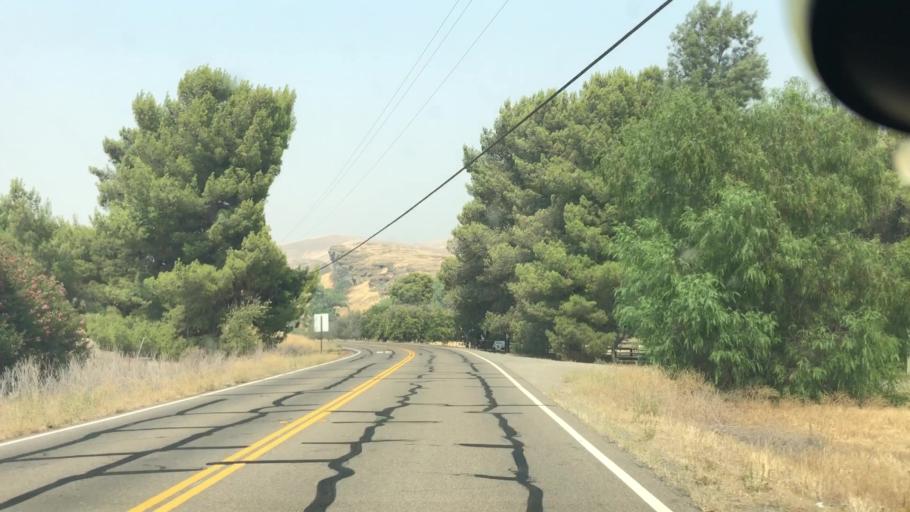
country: US
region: California
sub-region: San Joaquin County
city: Tracy
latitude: 37.6349
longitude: -121.4949
